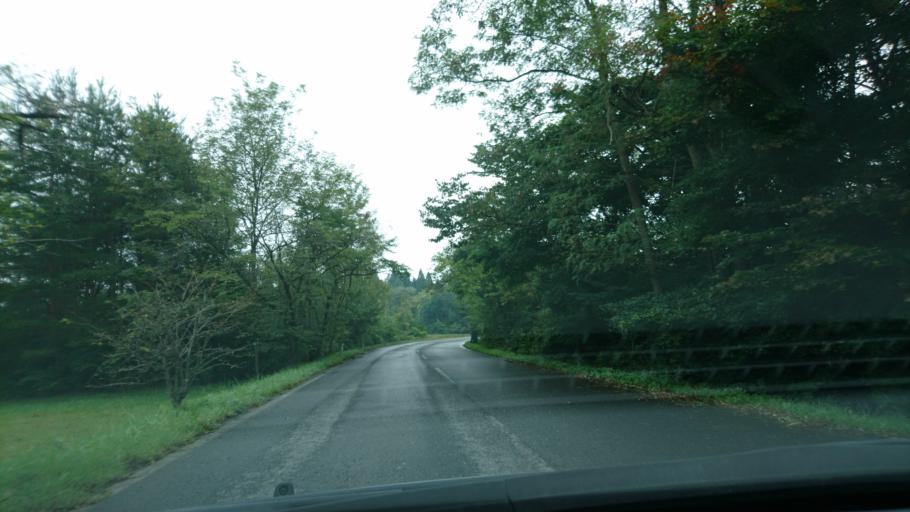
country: JP
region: Iwate
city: Ichinoseki
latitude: 38.9354
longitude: 141.1991
